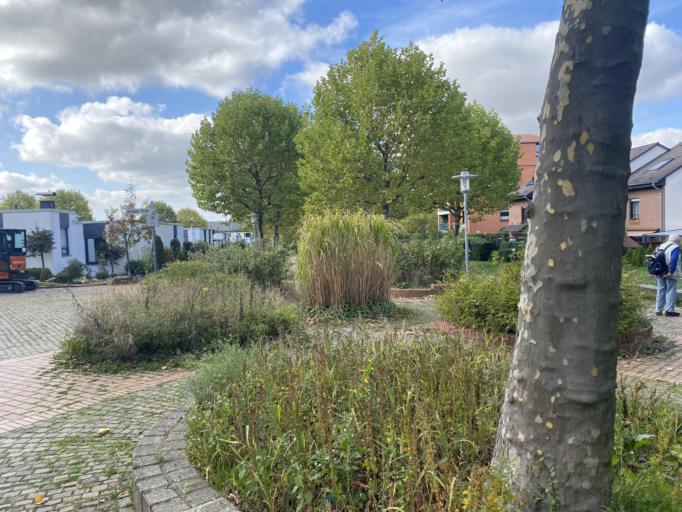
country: DE
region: North Rhine-Westphalia
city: Meckenheim
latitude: 50.6256
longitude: 7.0360
